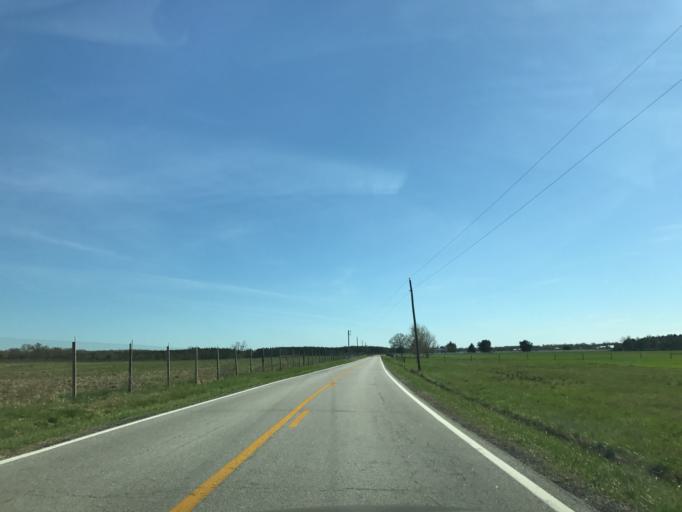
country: US
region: Maryland
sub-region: Caroline County
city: Ridgely
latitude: 38.9548
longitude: -75.9784
